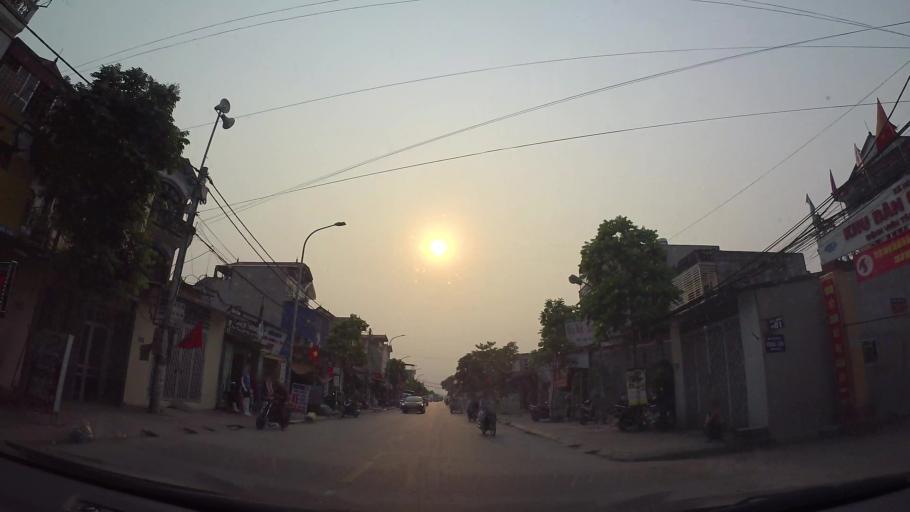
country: VN
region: Ha Noi
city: Thuong Tin
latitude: 20.8687
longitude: 105.8420
